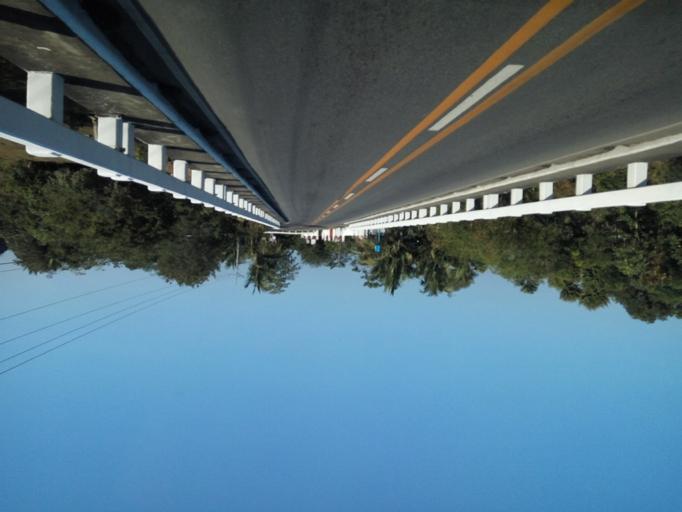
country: PH
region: Cagayan Valley
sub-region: Province of Cagayan
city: Amulung
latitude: 17.8214
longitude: 121.7263
